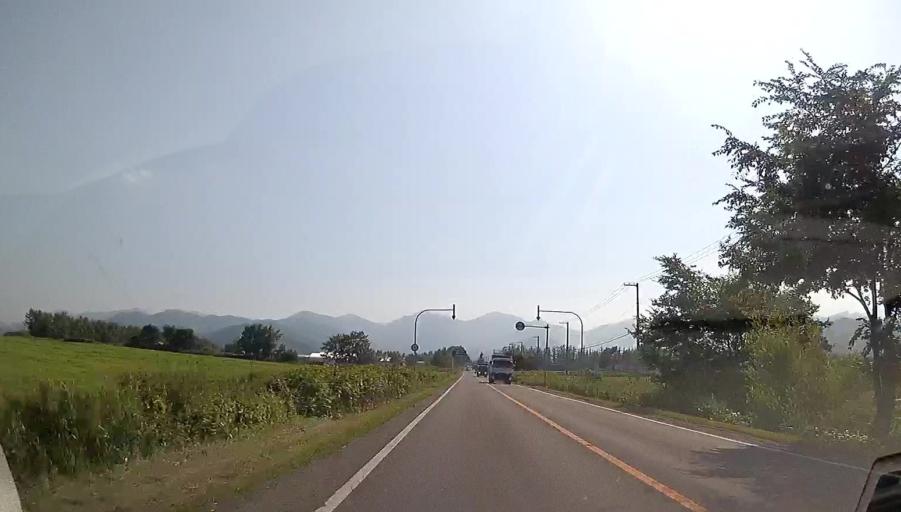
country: JP
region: Hokkaido
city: Otofuke
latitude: 43.0004
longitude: 142.8615
